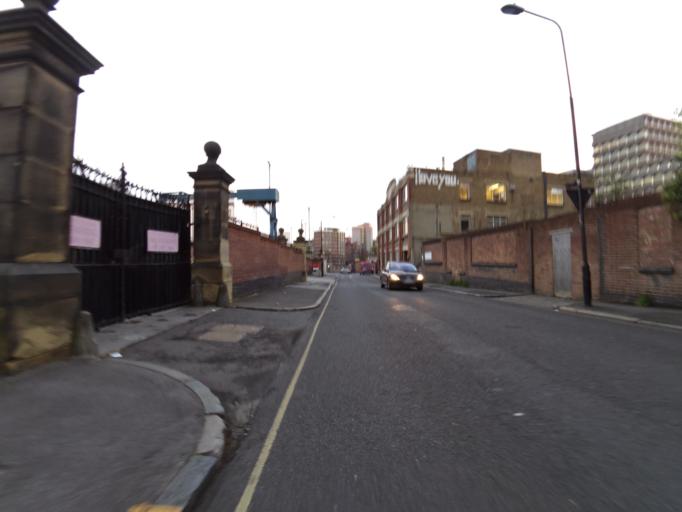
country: GB
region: England
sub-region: Greater London
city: Clerkenwell
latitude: 51.5253
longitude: -0.1141
